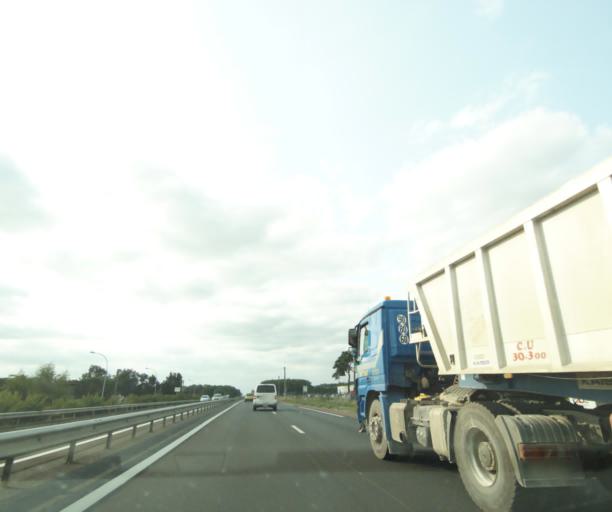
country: FR
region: Centre
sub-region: Departement d'Indre-et-Loire
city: Esvres
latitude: 47.3014
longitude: 0.7961
